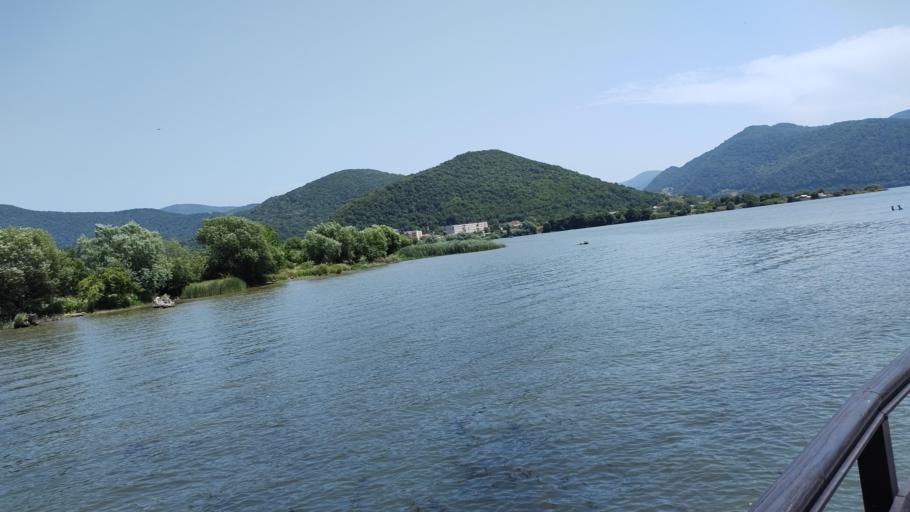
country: RO
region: Caras-Severin
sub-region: Comuna Berzasca
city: Berzasca
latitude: 44.6466
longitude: 21.9419
